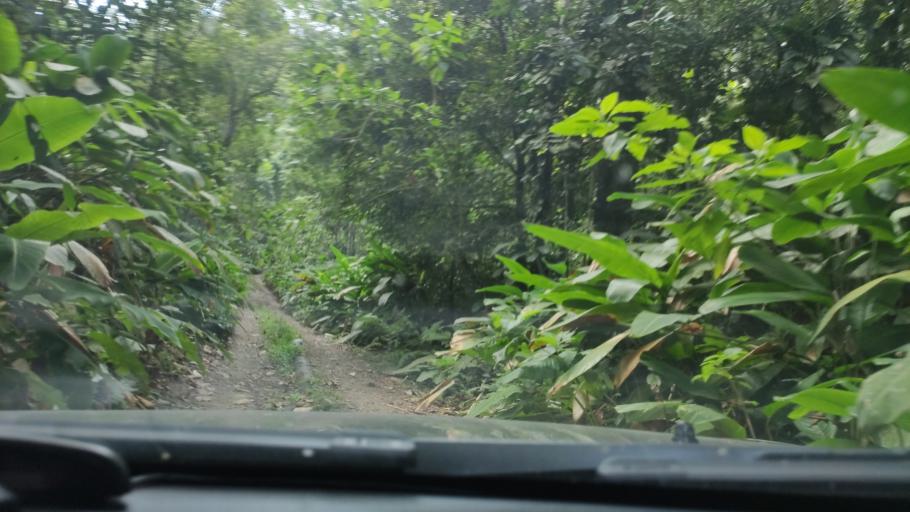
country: BR
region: Sao Paulo
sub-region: Sao Sebastiao
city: Sao Sebastiao
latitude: -23.7374
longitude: -45.4911
